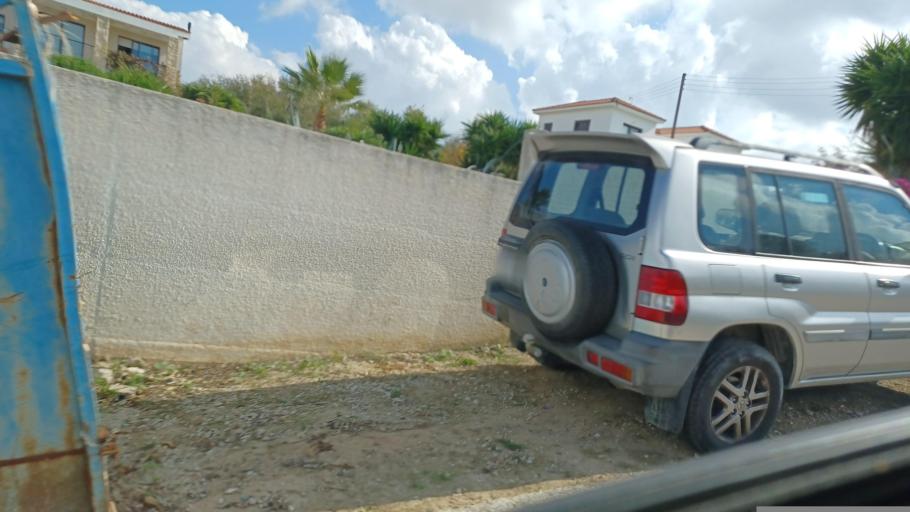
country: CY
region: Pafos
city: Mesogi
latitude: 34.8495
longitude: 32.5224
